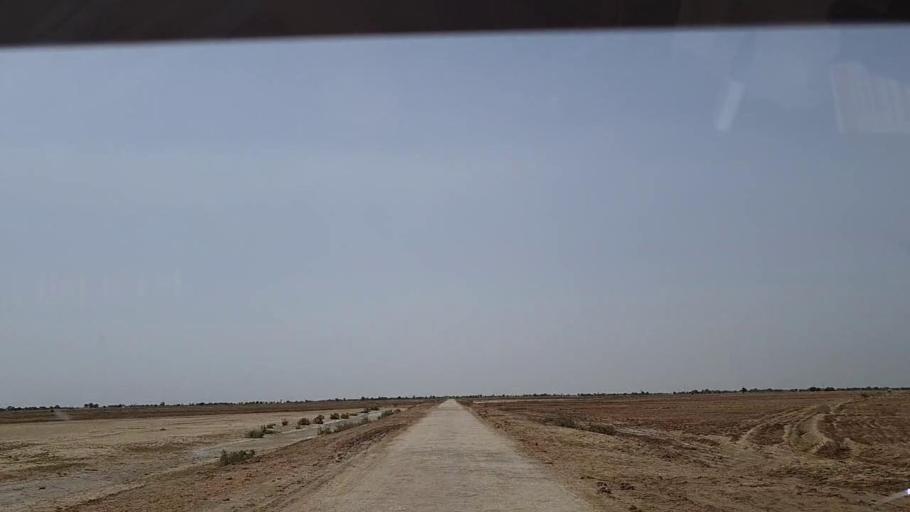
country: PK
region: Sindh
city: Johi
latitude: 26.7456
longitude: 67.6276
